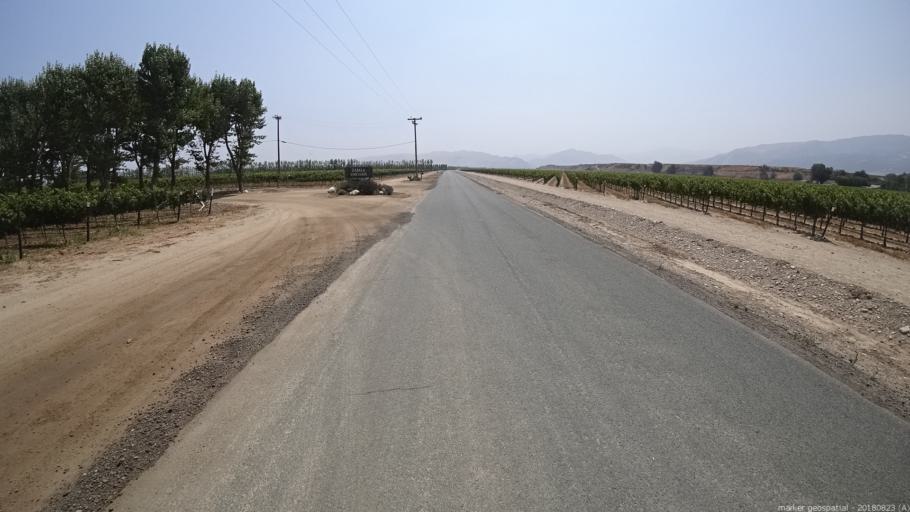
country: US
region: California
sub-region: Monterey County
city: Greenfield
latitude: 36.3448
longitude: -121.2985
